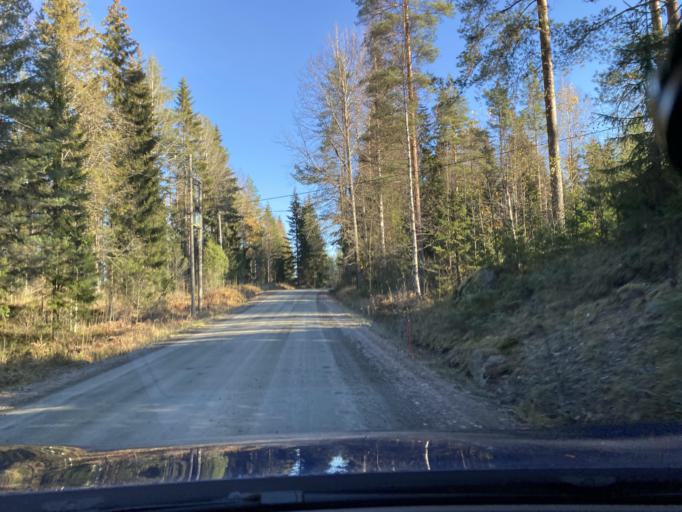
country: FI
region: Haeme
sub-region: Haemeenlinna
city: Kalvola
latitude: 60.9977
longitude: 24.1052
